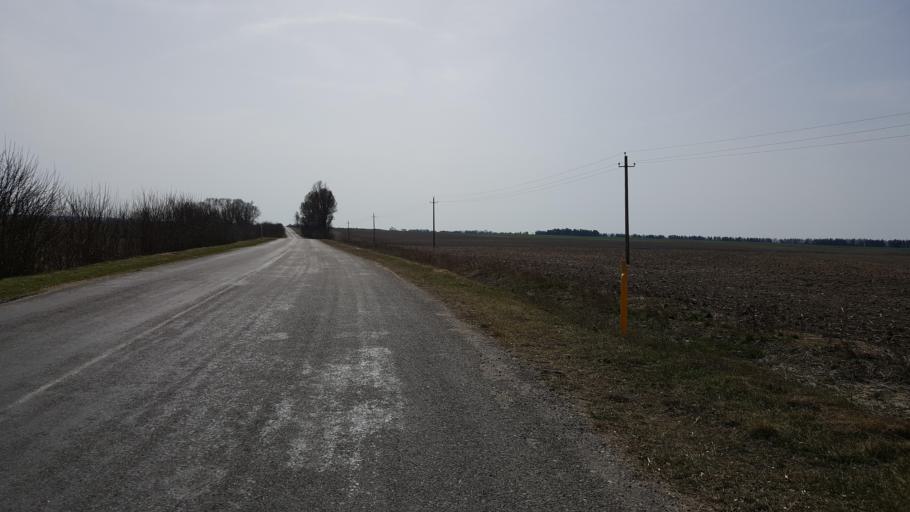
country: BY
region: Brest
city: Kamyanyets
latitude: 52.4250
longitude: 23.8103
